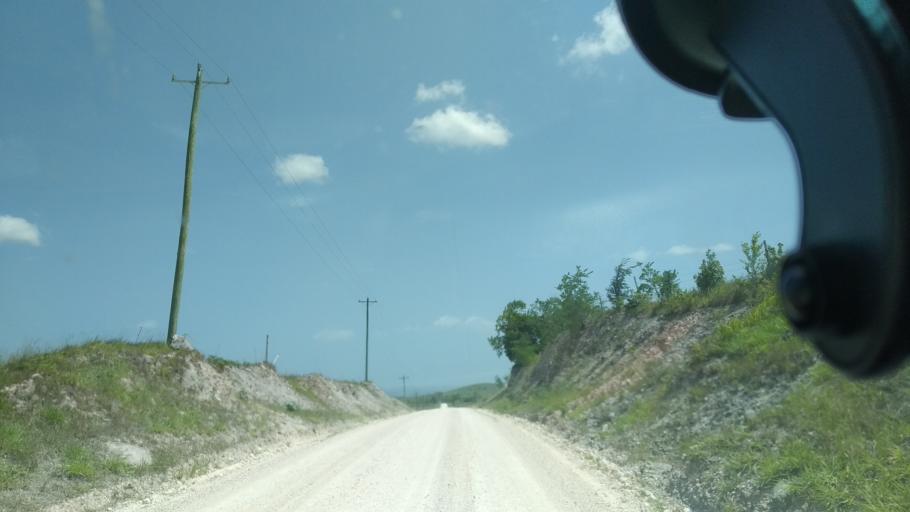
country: BZ
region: Cayo
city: San Ignacio
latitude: 17.3049
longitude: -89.0480
